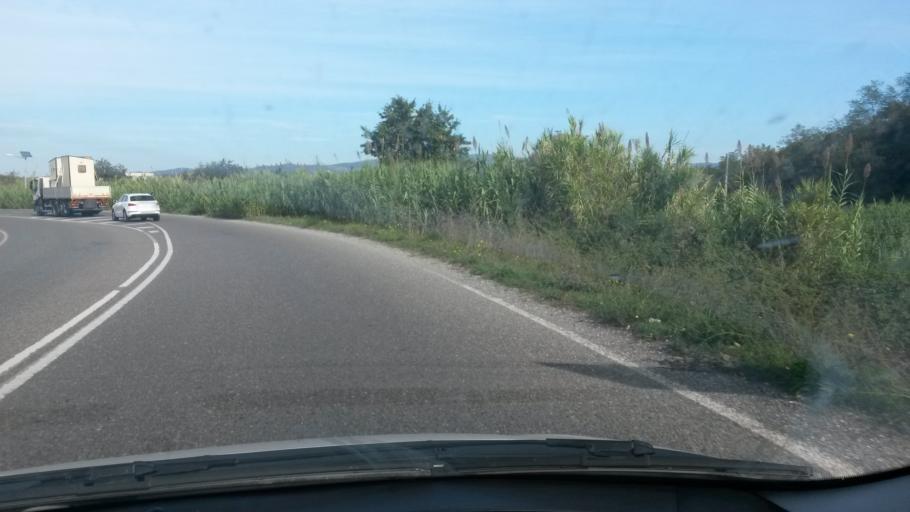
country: IT
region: Tuscany
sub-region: Provincia di Livorno
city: Cecina
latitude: 43.3183
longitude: 10.5355
